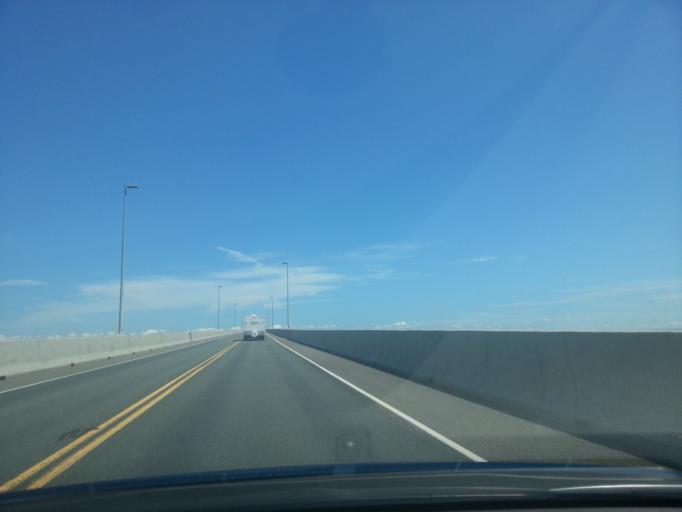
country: CA
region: Prince Edward Island
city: Summerside
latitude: 46.1683
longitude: -63.8091
